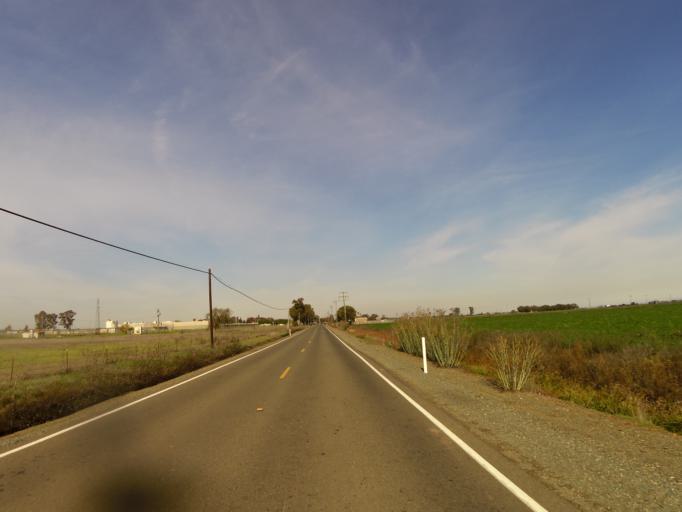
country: US
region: California
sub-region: San Joaquin County
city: Thornton
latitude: 38.3007
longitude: -121.4200
